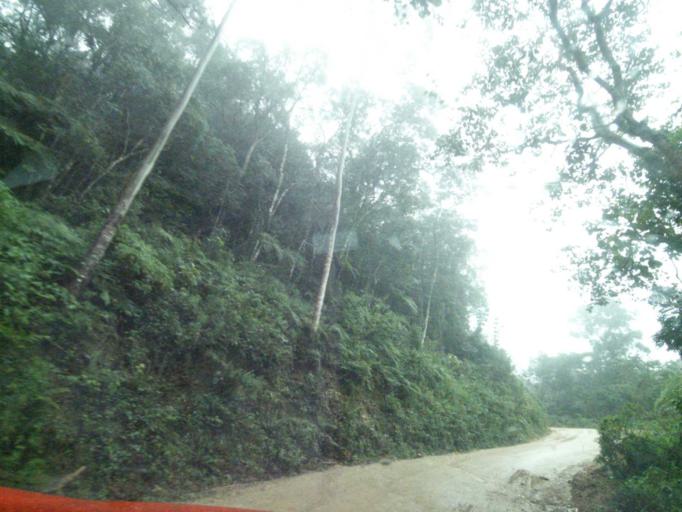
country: BR
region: Santa Catarina
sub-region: Anitapolis
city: Anitapolis
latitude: -27.8928
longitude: -49.1923
